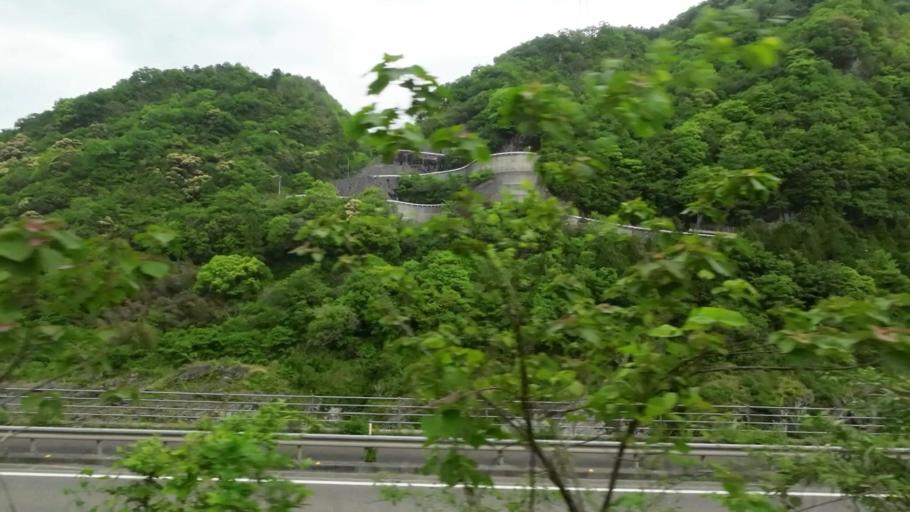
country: JP
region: Tokushima
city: Ikedacho
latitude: 33.9795
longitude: 133.7853
